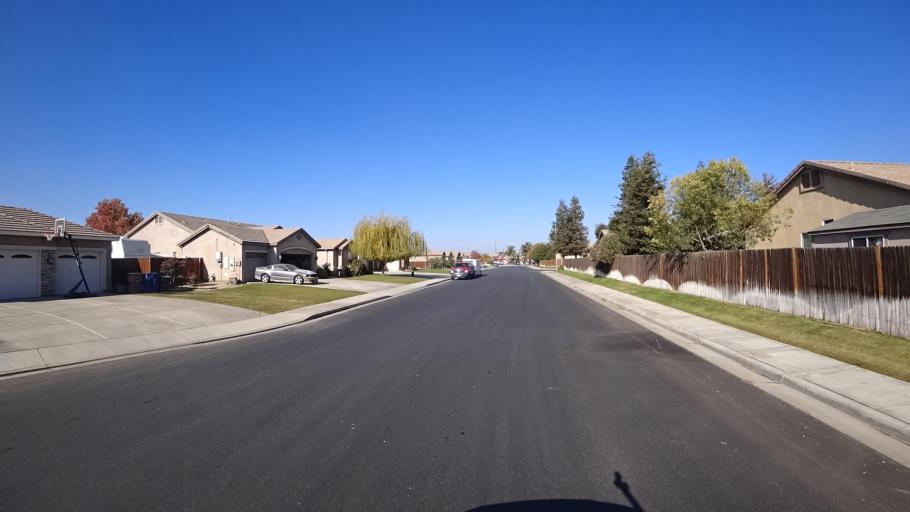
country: US
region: California
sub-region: Kern County
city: Greenfield
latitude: 35.2929
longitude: -119.0736
